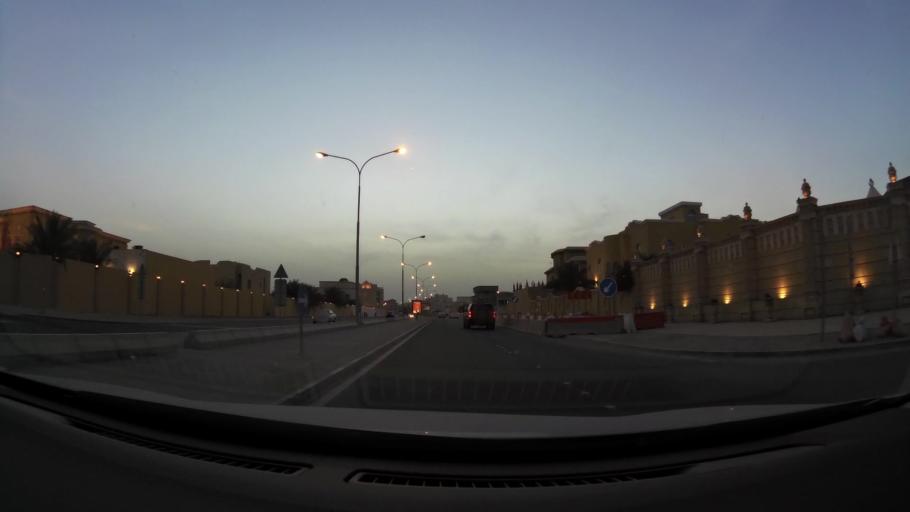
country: QA
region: Al Wakrah
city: Al Wakrah
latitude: 25.1618
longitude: 51.6063
